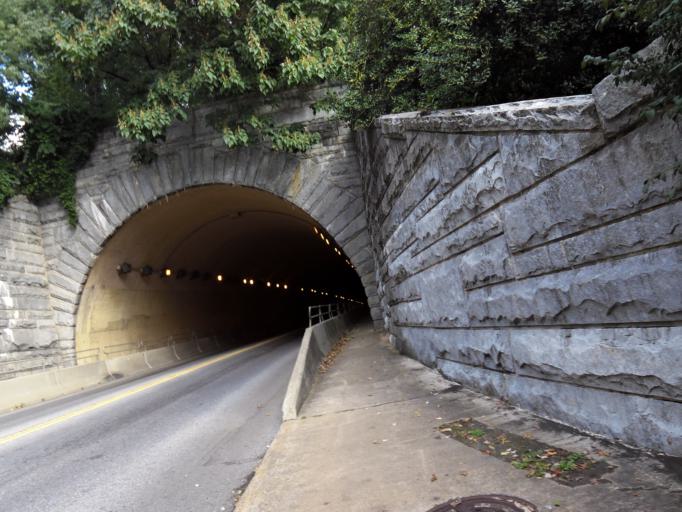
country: US
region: North Carolina
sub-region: Buncombe County
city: Asheville
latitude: 35.5992
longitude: -82.5404
